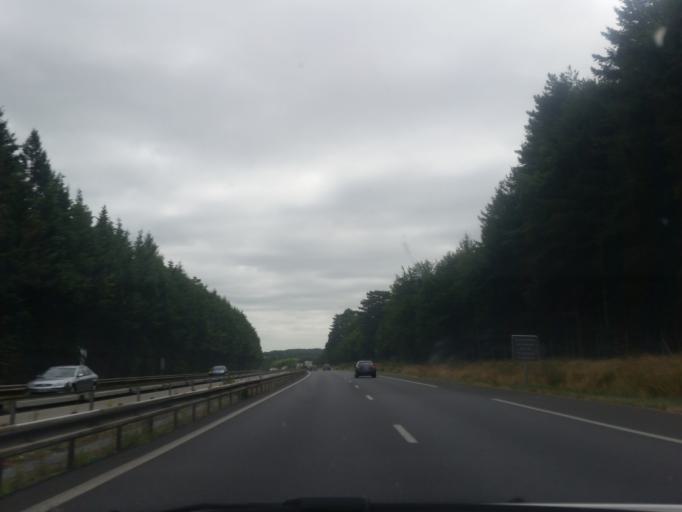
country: FR
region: Pays de la Loire
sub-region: Departement de la Loire-Atlantique
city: Carquefou
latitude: 47.2913
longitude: -1.4673
